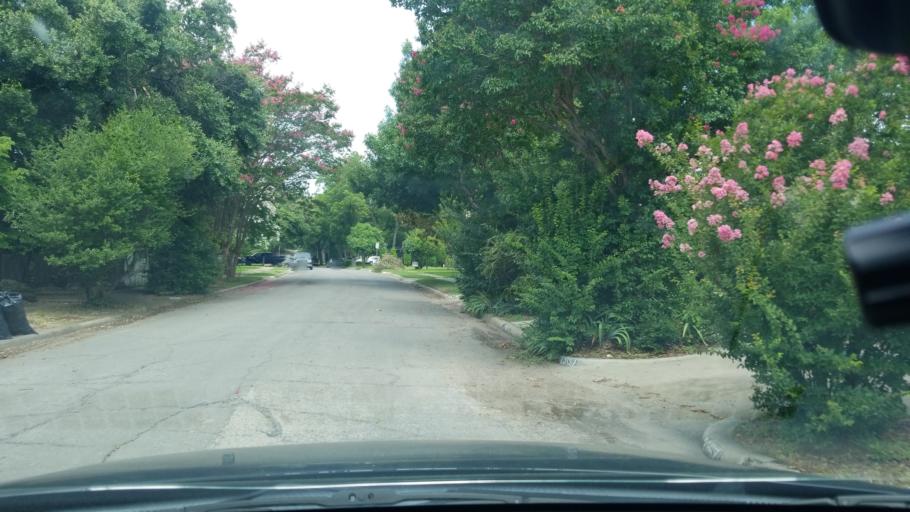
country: US
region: Texas
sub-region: Dallas County
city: Garland
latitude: 32.8298
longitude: -96.6757
